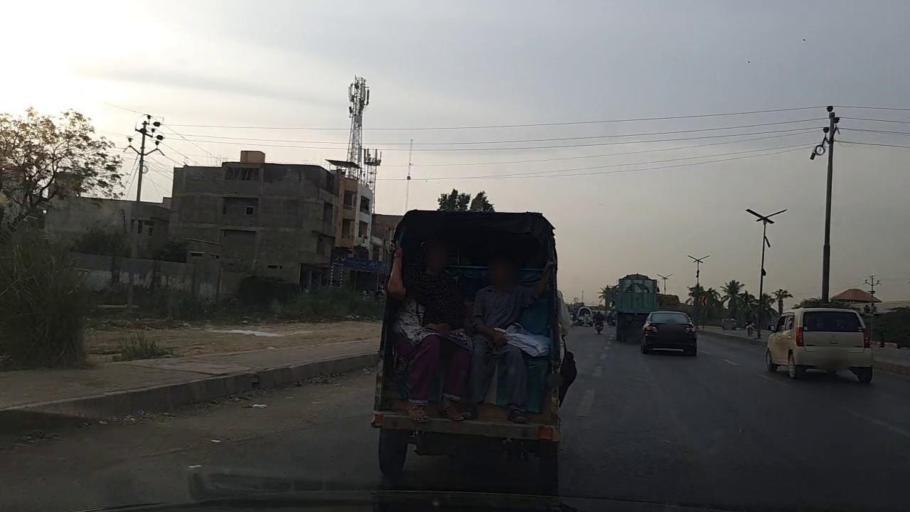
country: PK
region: Sindh
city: Malir Cantonment
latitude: 24.8539
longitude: 67.2449
